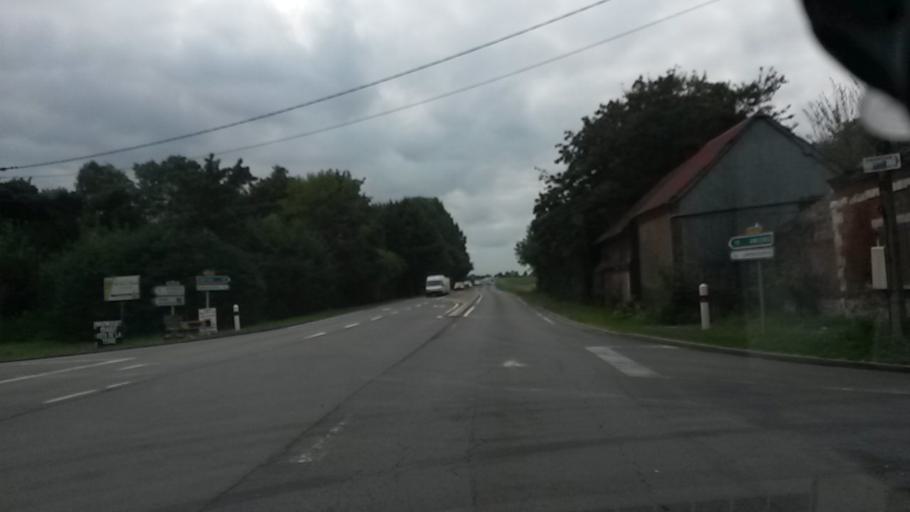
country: FR
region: Picardie
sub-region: Departement de la Somme
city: Corbie
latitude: 49.9595
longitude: 2.5029
